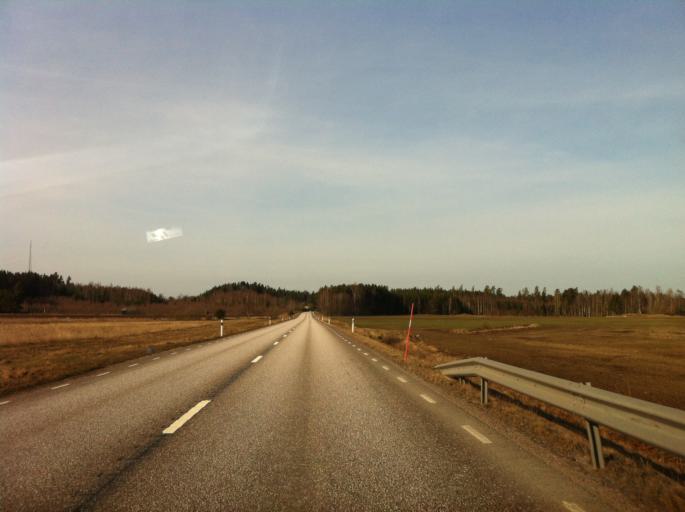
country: SE
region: Vaestra Goetaland
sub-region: Skovde Kommun
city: Skultorp
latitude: 58.2376
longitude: 13.8274
